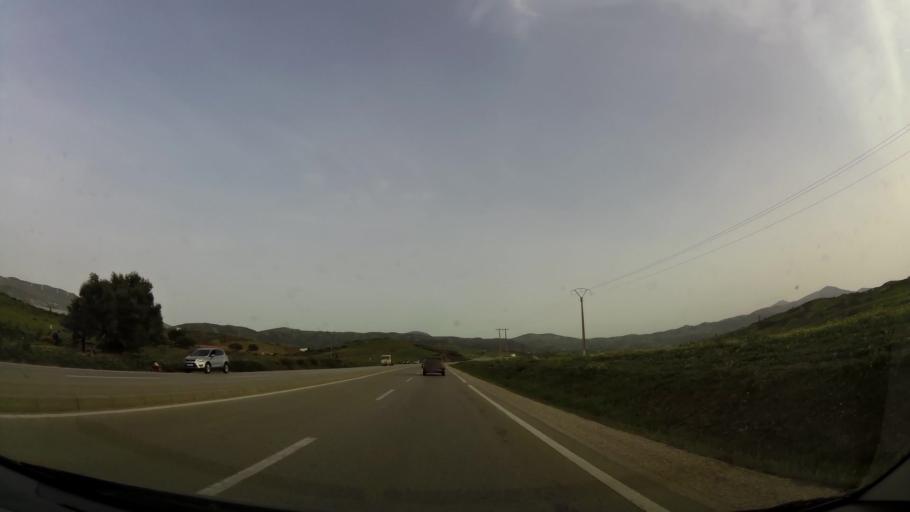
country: MA
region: Tanger-Tetouan
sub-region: Tanger-Assilah
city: Dar Chaoui
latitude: 35.5731
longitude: -5.6265
